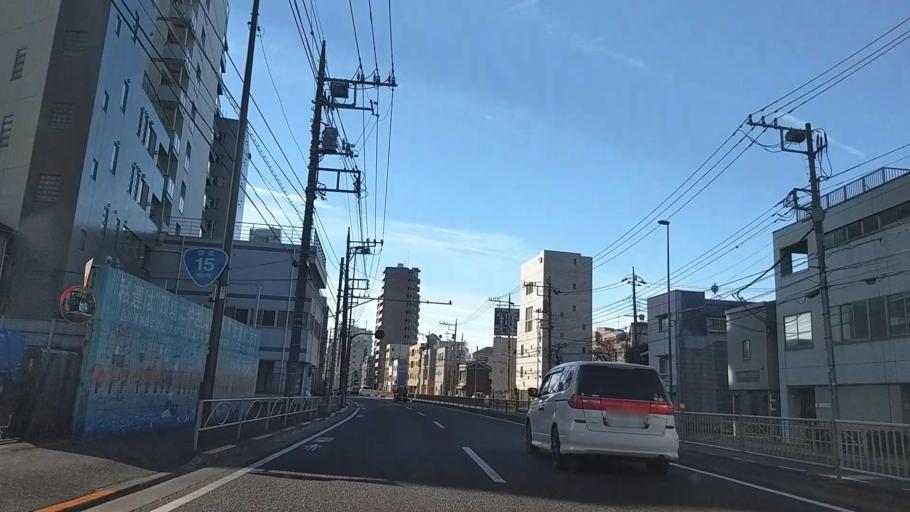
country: JP
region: Kanagawa
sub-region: Kawasaki-shi
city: Kawasaki
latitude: 35.6031
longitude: 139.7405
